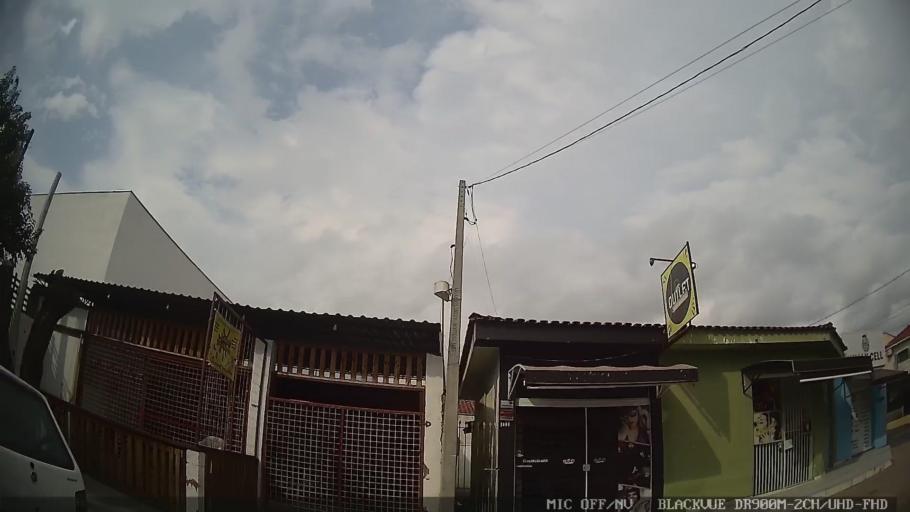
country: BR
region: Sao Paulo
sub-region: Indaiatuba
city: Indaiatuba
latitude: -23.1137
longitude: -47.2401
